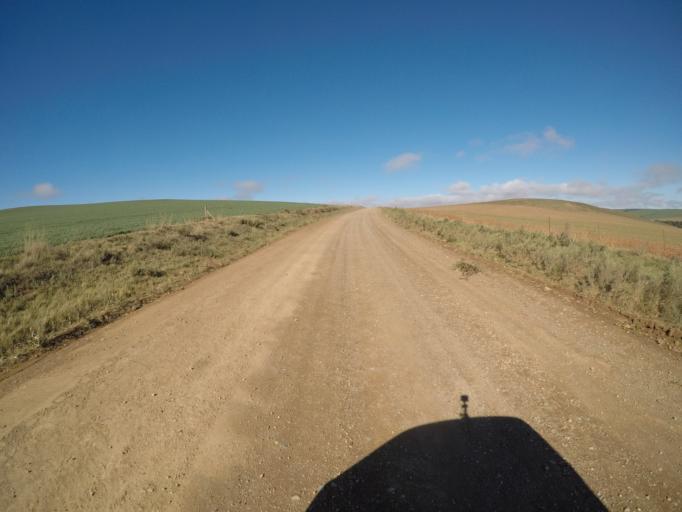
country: ZA
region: Western Cape
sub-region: Overberg District Municipality
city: Caledon
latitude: -34.1122
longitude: 19.7095
